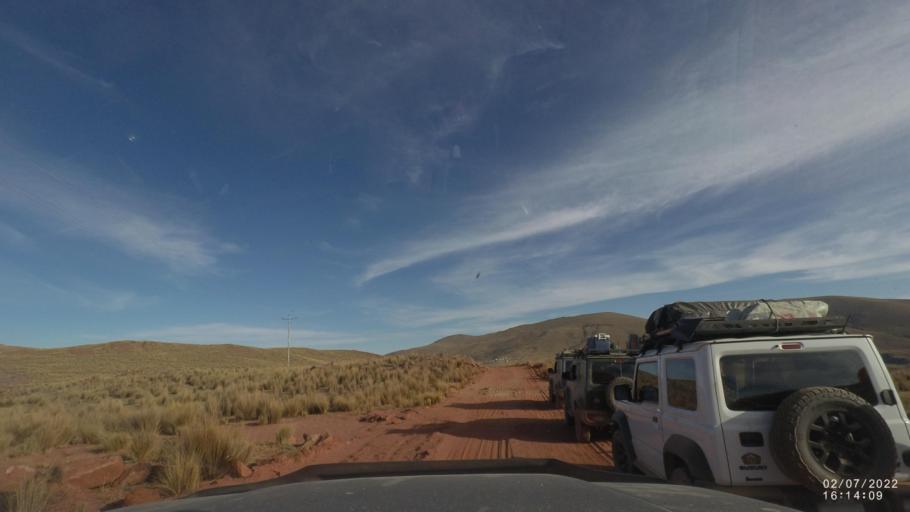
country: BO
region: Cochabamba
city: Irpa Irpa
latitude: -17.9137
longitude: -66.4401
